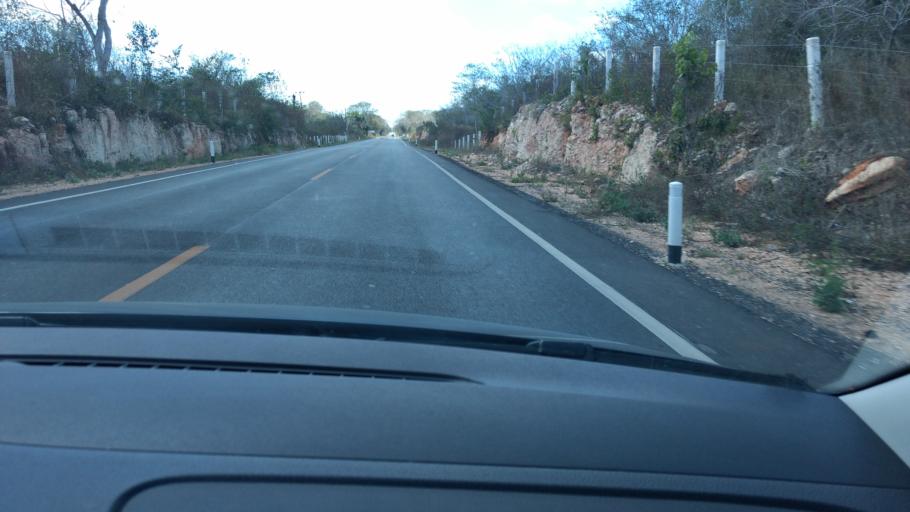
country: MX
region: Yucatan
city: Peto
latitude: 20.1134
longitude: -88.9584
